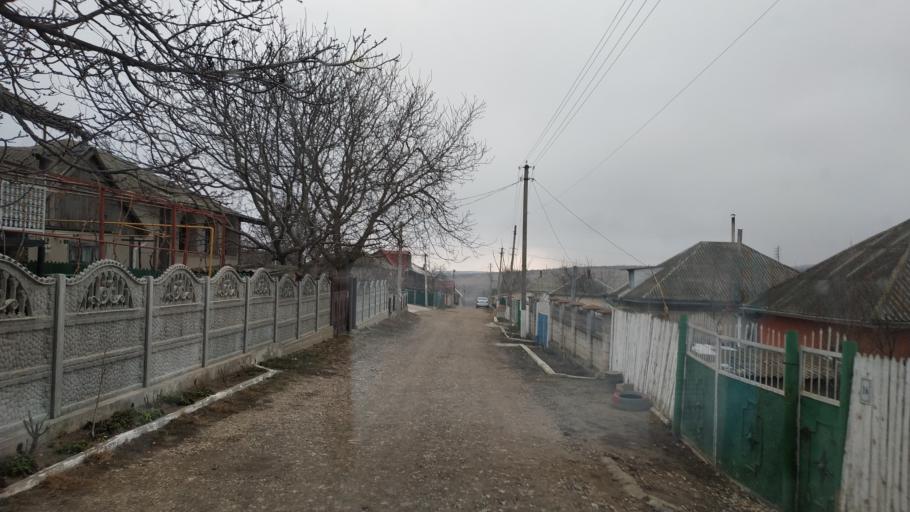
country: MD
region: Laloveni
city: Ialoveni
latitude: 46.8892
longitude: 28.6906
